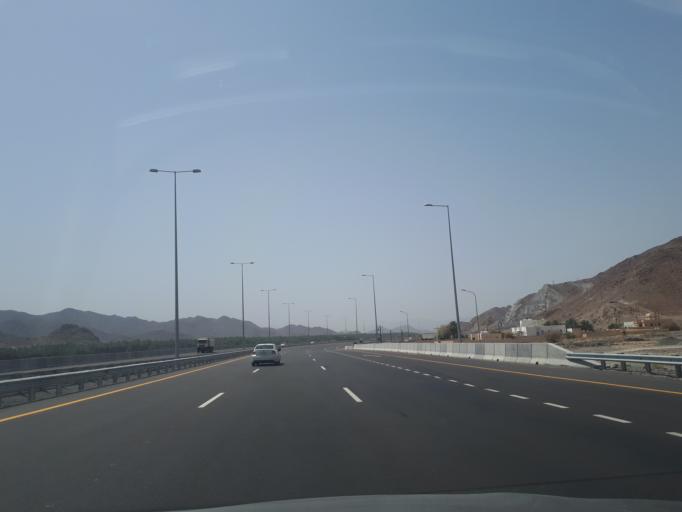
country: OM
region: Muhafazat ad Dakhiliyah
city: Bidbid
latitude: 23.3816
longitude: 58.1031
